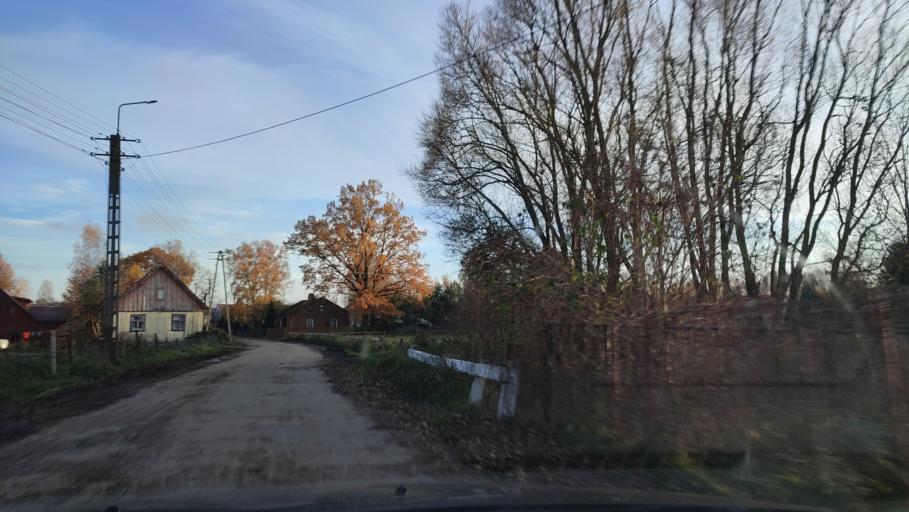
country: PL
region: Masovian Voivodeship
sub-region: Powiat mlawski
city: Dzierzgowo
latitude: 53.2776
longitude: 20.6479
